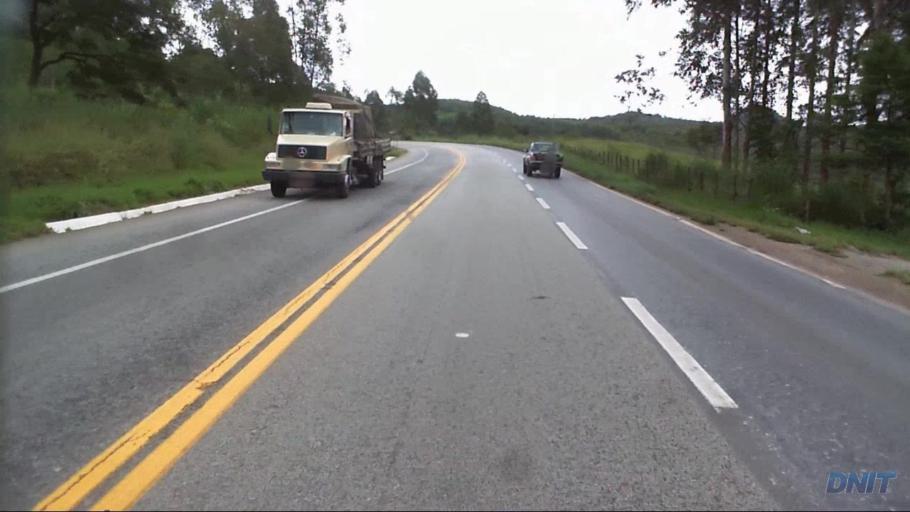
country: BR
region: Minas Gerais
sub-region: Caete
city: Caete
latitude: -19.7540
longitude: -43.5316
